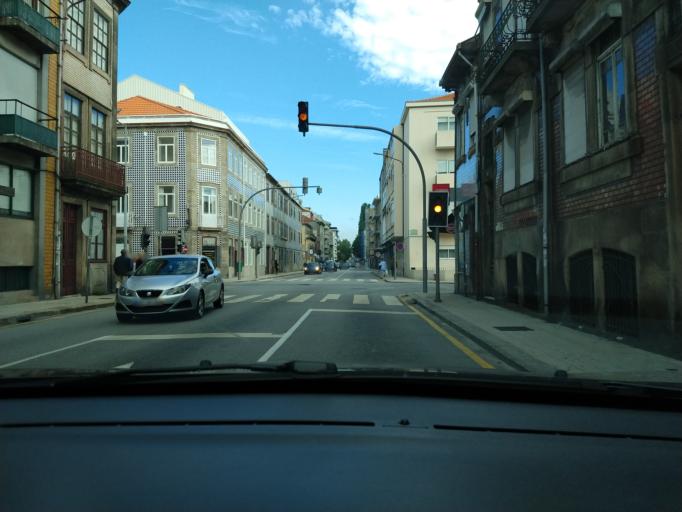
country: PT
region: Porto
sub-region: Porto
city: Porto
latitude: 41.1591
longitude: -8.6012
